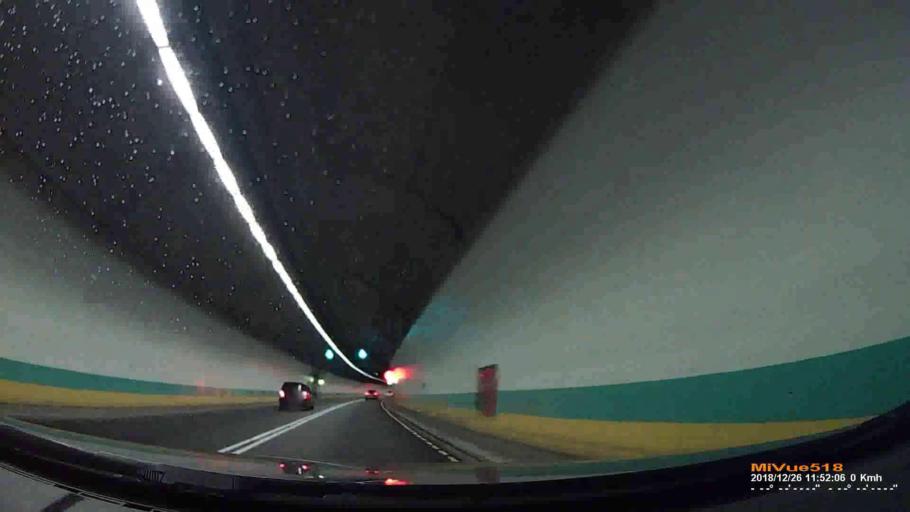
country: TW
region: Taipei
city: Taipei
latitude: 24.9696
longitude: 121.6820
